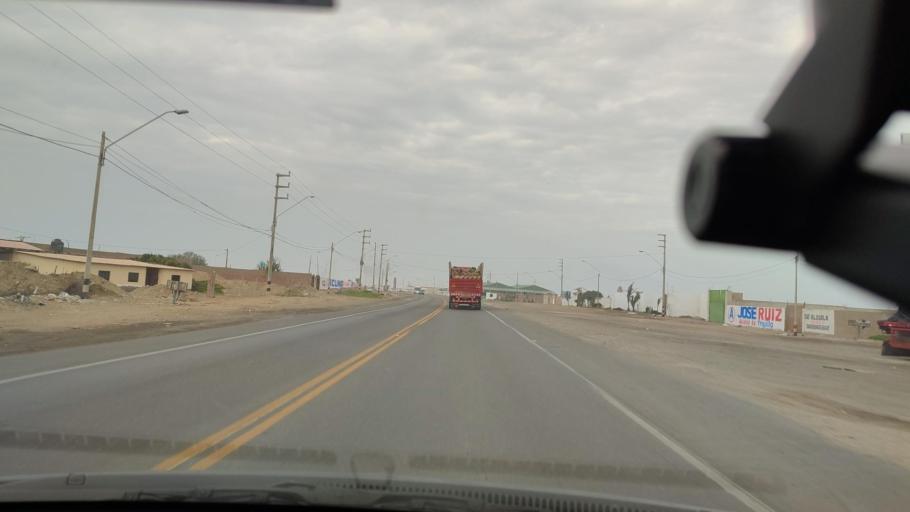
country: PE
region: La Libertad
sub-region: Provincia de Trujillo
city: Huanchaco
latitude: -8.0963
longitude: -79.0988
